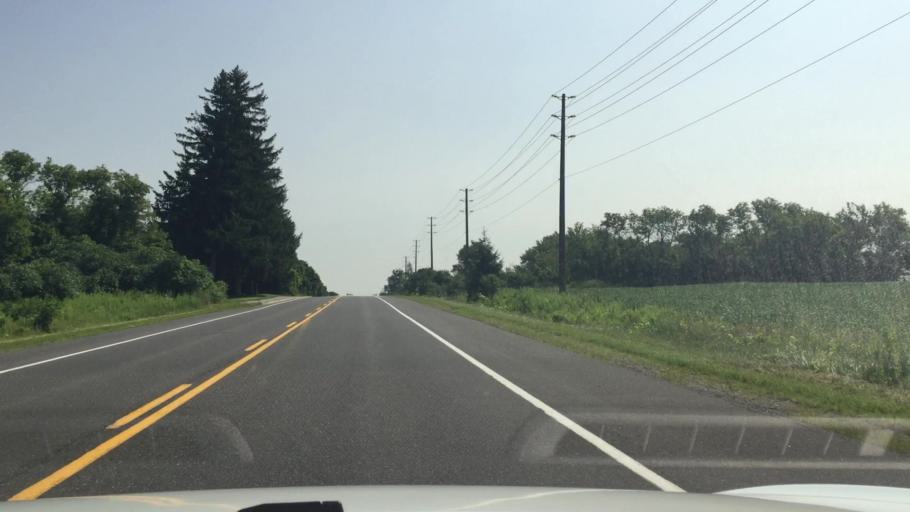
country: CA
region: Ontario
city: Pickering
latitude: 43.9066
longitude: -79.1603
